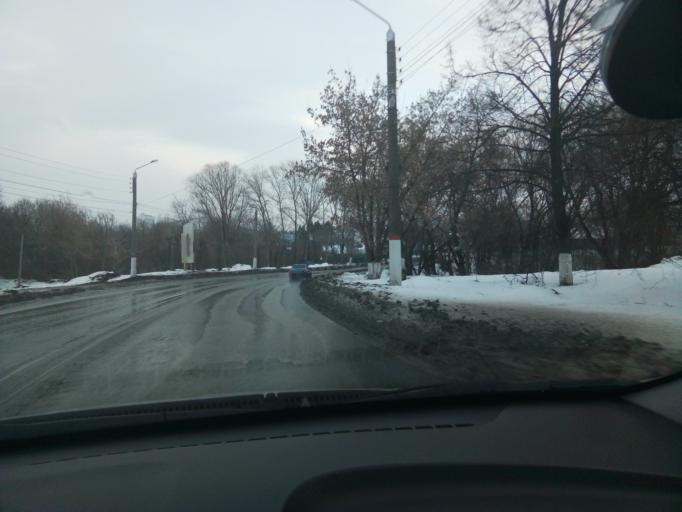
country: RU
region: Chuvashia
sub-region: Cheboksarskiy Rayon
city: Cheboksary
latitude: 56.1349
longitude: 47.2248
